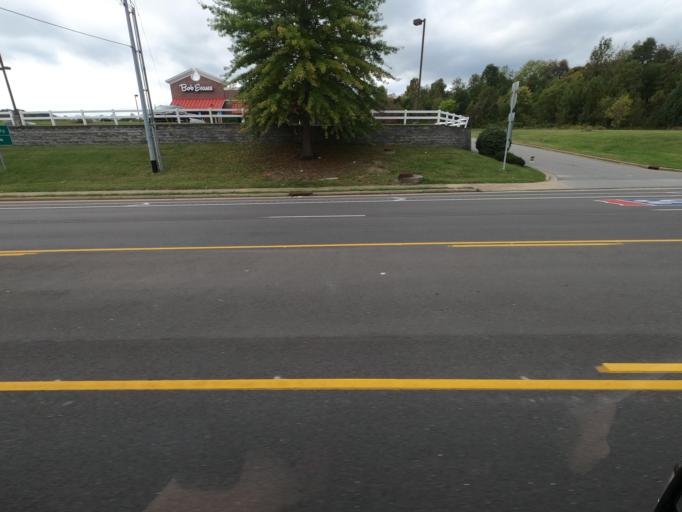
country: US
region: Tennessee
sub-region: Washington County
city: Oak Grove
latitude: 36.3801
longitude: -82.4248
